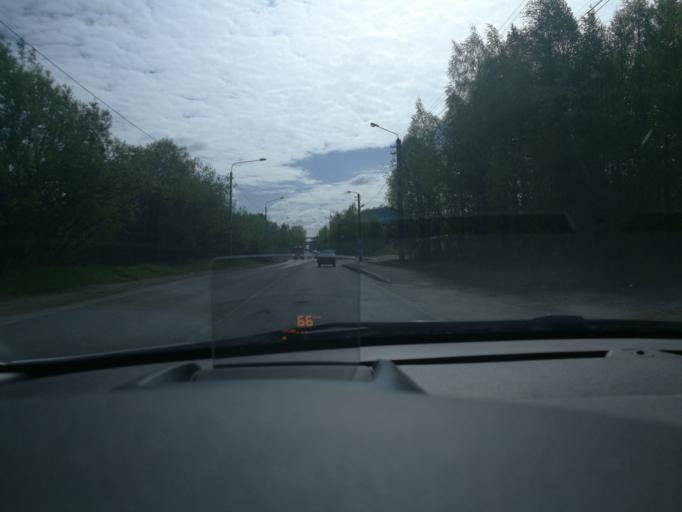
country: RU
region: Arkhangelskaya
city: Arkhangel'sk
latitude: 64.5973
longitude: 40.5627
